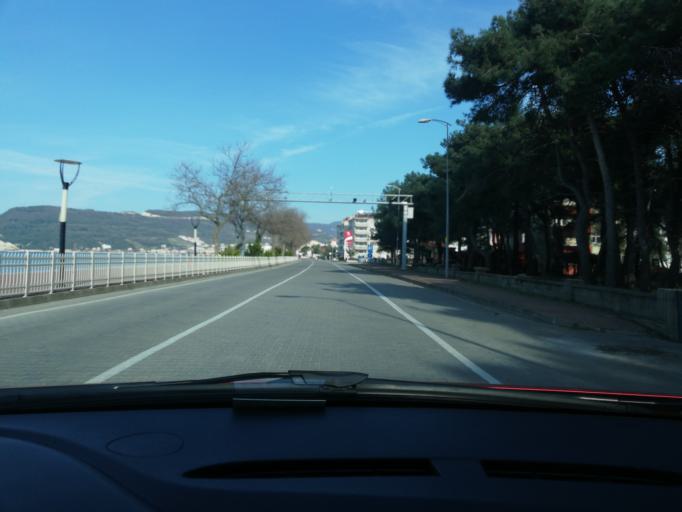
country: TR
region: Kastamonu
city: Cide
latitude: 41.8884
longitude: 32.9657
